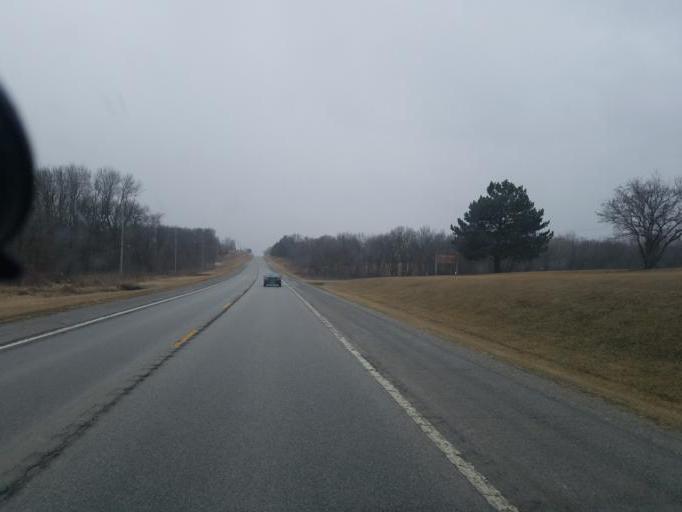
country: US
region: Missouri
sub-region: Schuyler County
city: Lancaster
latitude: 40.3608
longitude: -92.5633
